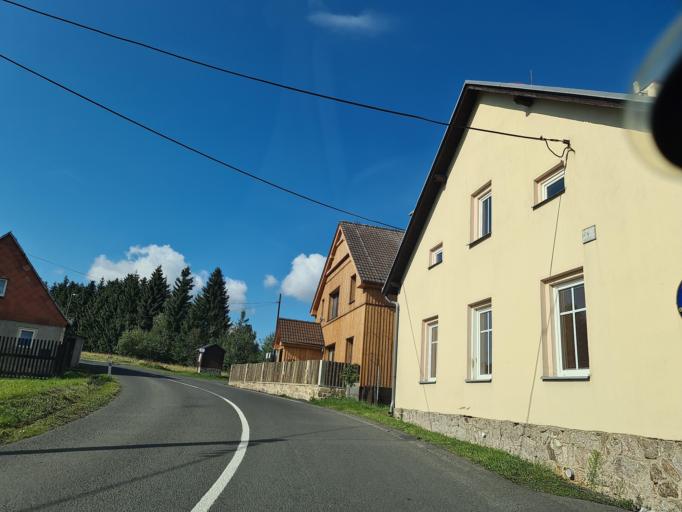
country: CZ
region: Ustecky
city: Mezibori
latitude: 50.6350
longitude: 13.5572
